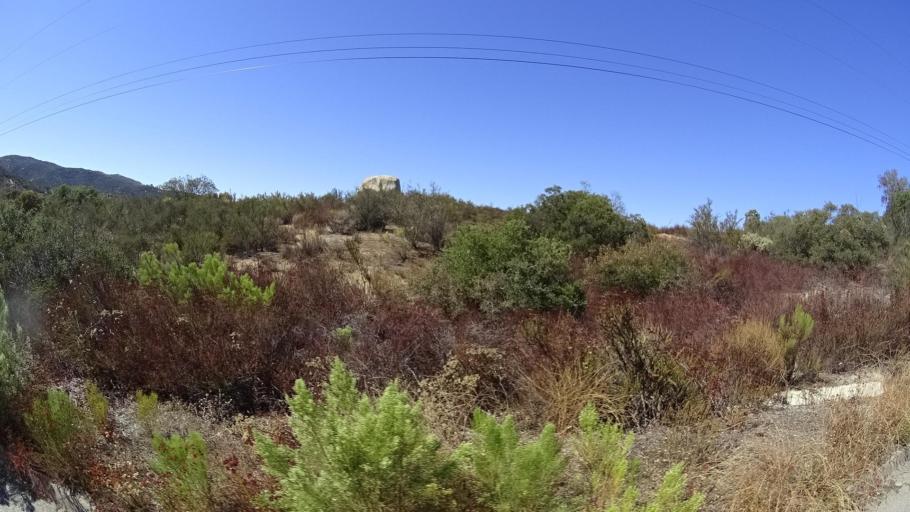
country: US
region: California
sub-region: San Diego County
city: Alpine
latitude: 32.7577
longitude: -116.7707
